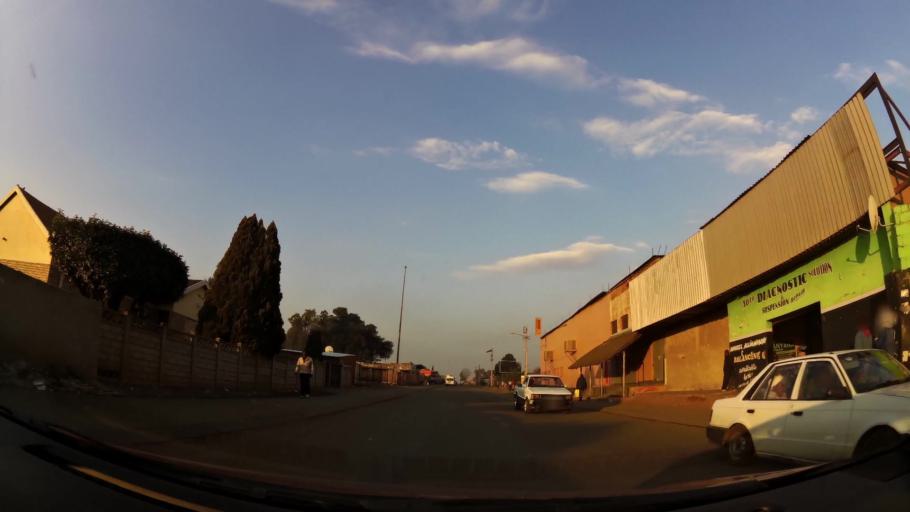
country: ZA
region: Gauteng
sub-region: City of Johannesburg Metropolitan Municipality
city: Orange Farm
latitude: -26.5342
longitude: 27.8492
